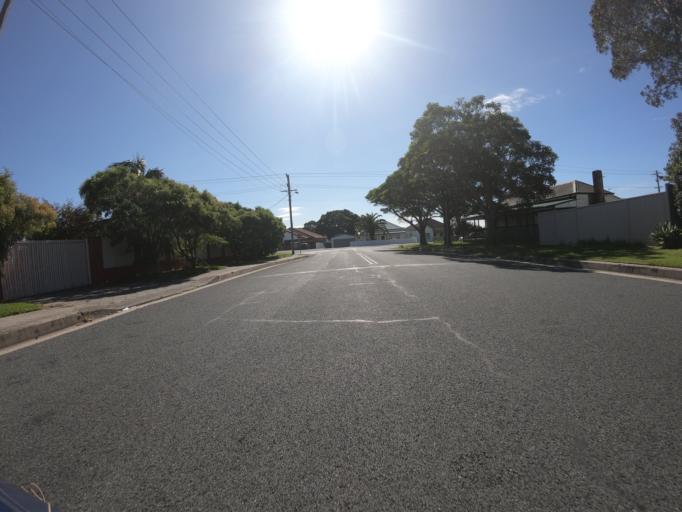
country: AU
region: New South Wales
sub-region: Wollongong
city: East Corrimal
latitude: -34.3682
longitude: 150.9086
